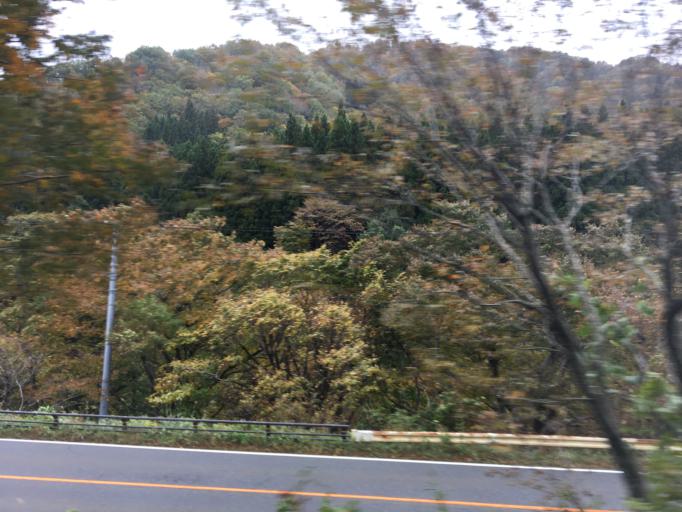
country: JP
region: Yamagata
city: Nagai
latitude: 38.0475
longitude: 139.8290
